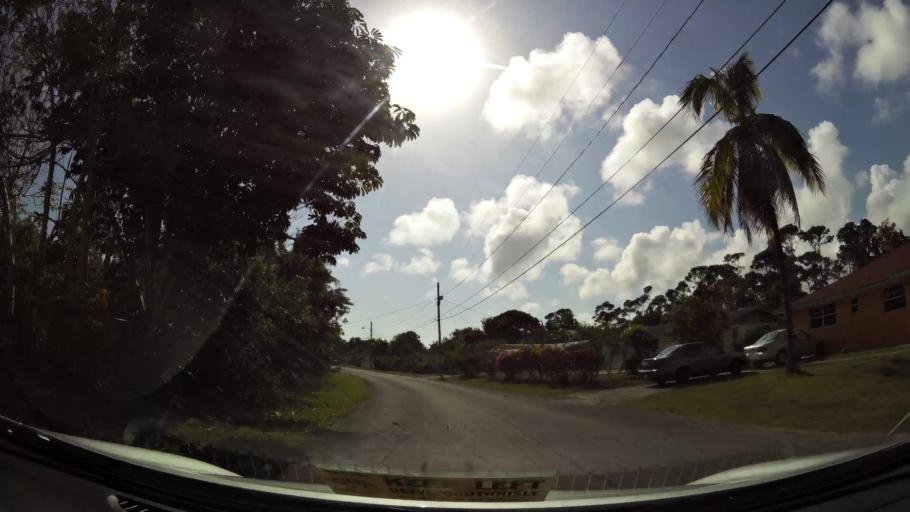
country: BS
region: Freeport
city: Freeport
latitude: 26.5233
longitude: -78.6848
